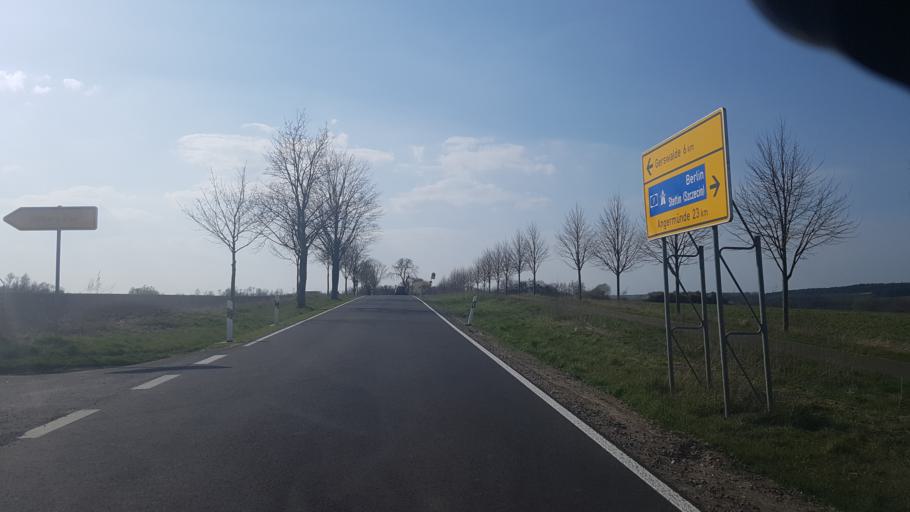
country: DE
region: Brandenburg
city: Gerswalde
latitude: 53.1599
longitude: 13.8280
